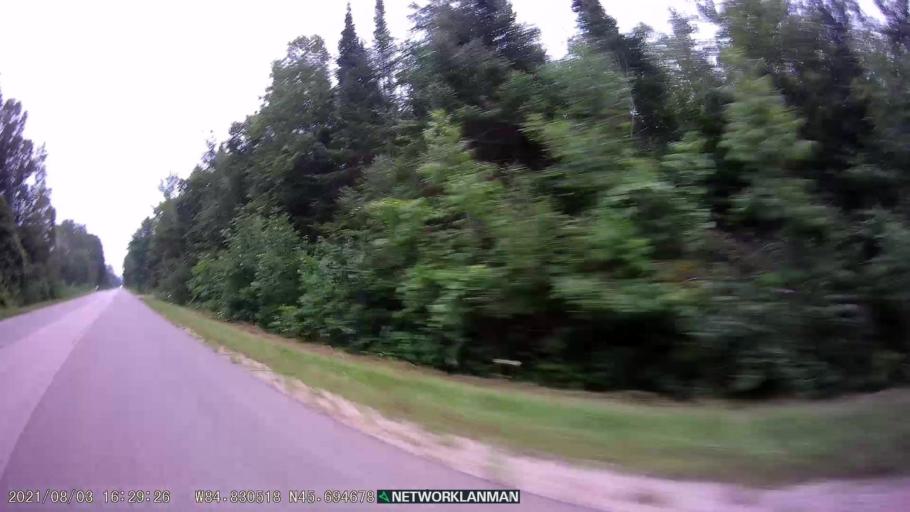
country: US
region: Michigan
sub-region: Mackinac County
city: Saint Ignace
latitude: 45.6948
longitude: -84.8308
